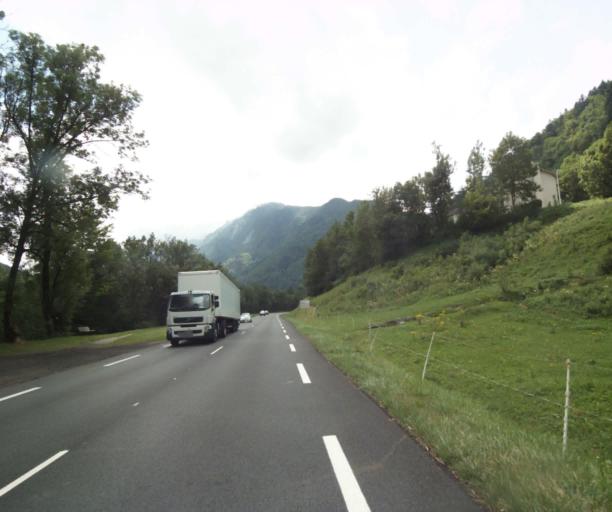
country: FR
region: Rhone-Alpes
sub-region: Departement de la Haute-Savoie
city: Thones
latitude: 45.8865
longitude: 6.3280
